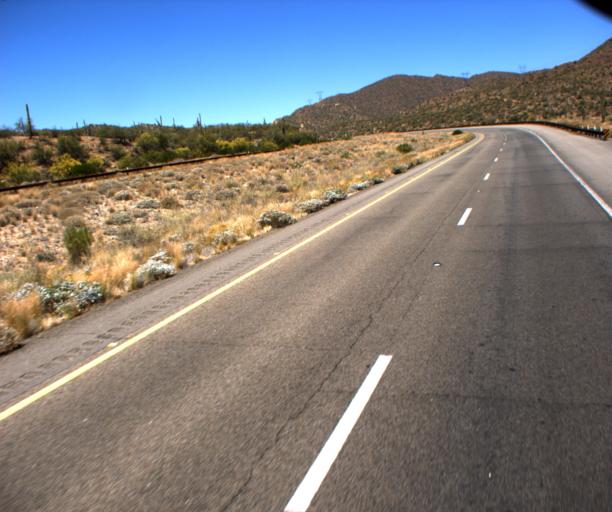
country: US
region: Arizona
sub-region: Yavapai County
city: Bagdad
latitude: 34.3924
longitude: -113.2091
